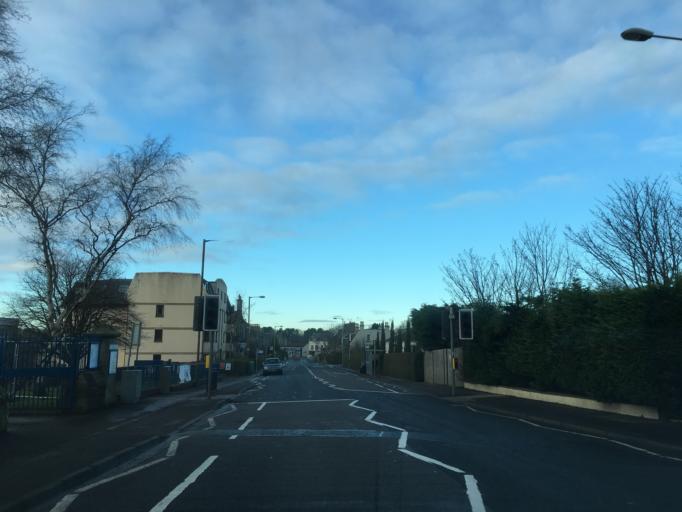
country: GB
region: Scotland
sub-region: Edinburgh
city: Colinton
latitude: 55.9641
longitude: -3.2669
